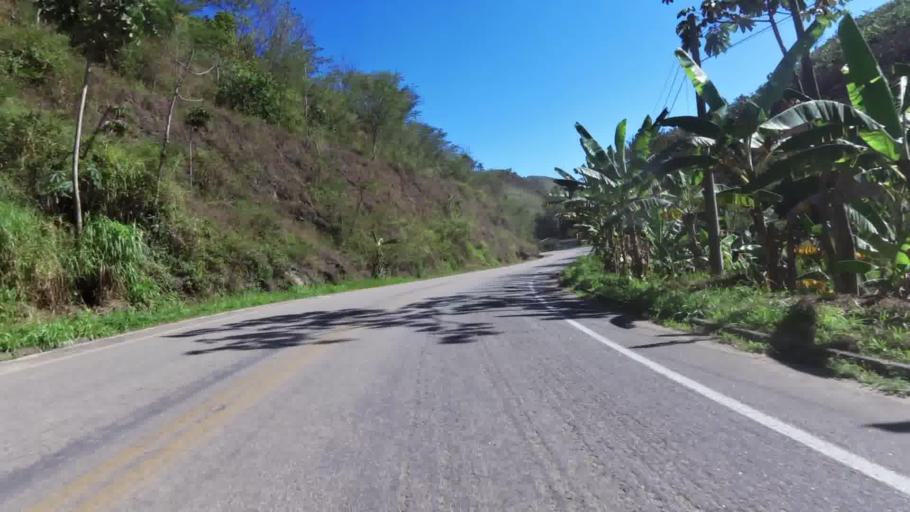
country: BR
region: Espirito Santo
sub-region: Iconha
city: Iconha
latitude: -20.7325
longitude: -40.8806
